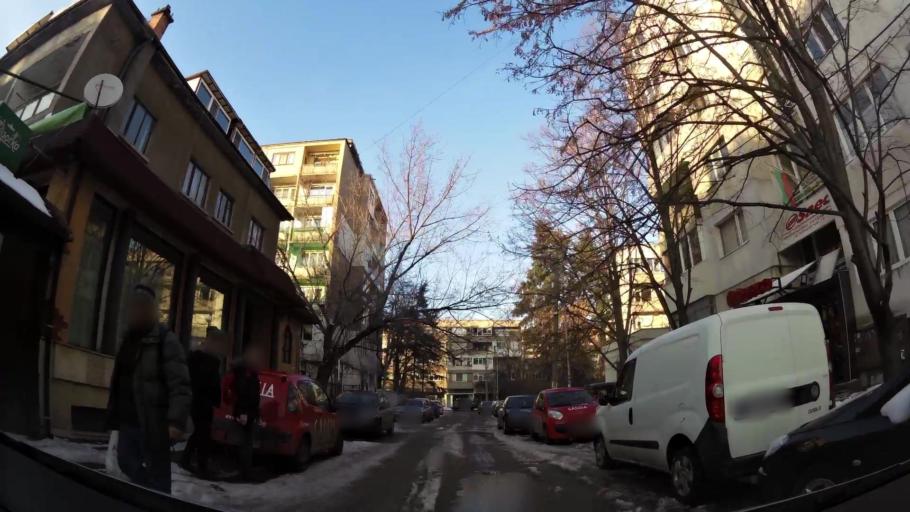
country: BG
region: Sofia-Capital
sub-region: Stolichna Obshtina
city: Sofia
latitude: 42.6822
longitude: 23.3643
